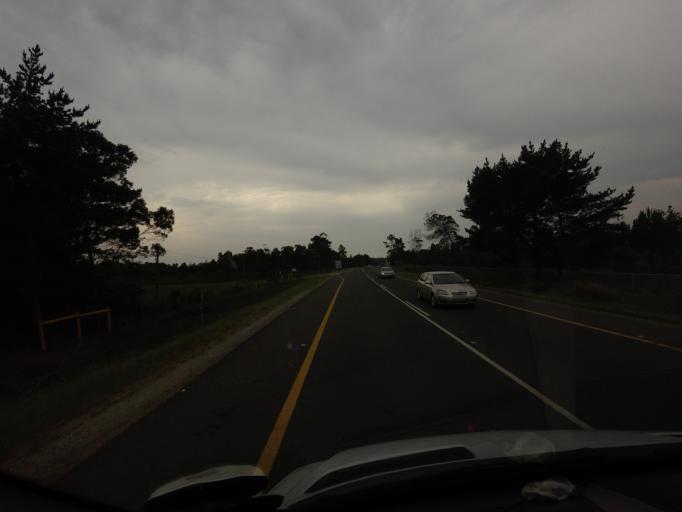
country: ZA
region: Western Cape
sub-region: Eden District Municipality
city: Plettenberg Bay
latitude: -34.0444
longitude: 23.3150
